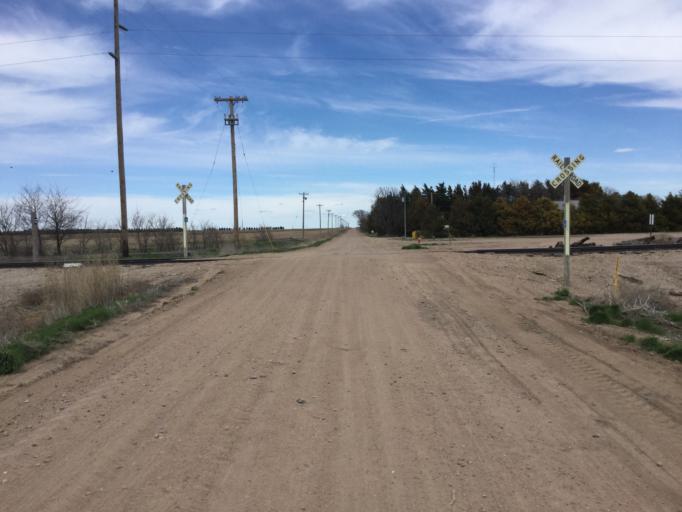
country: US
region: Kansas
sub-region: Sherman County
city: Goodland
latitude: 39.3401
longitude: -101.6887
